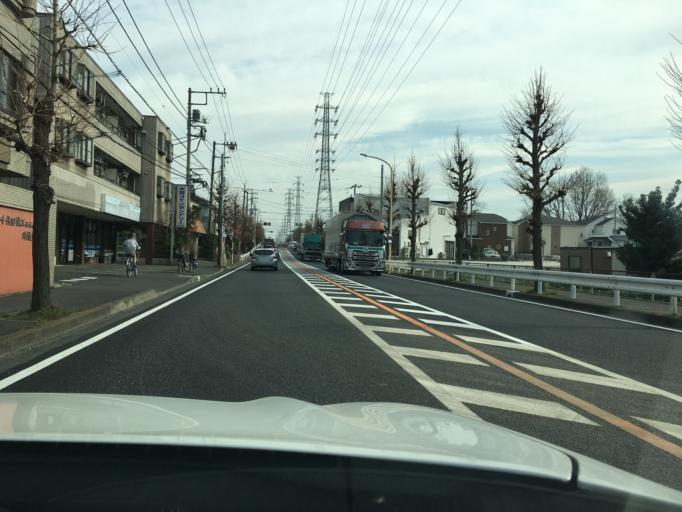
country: JP
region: Saitama
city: Kawagoe
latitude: 35.9093
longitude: 139.4712
